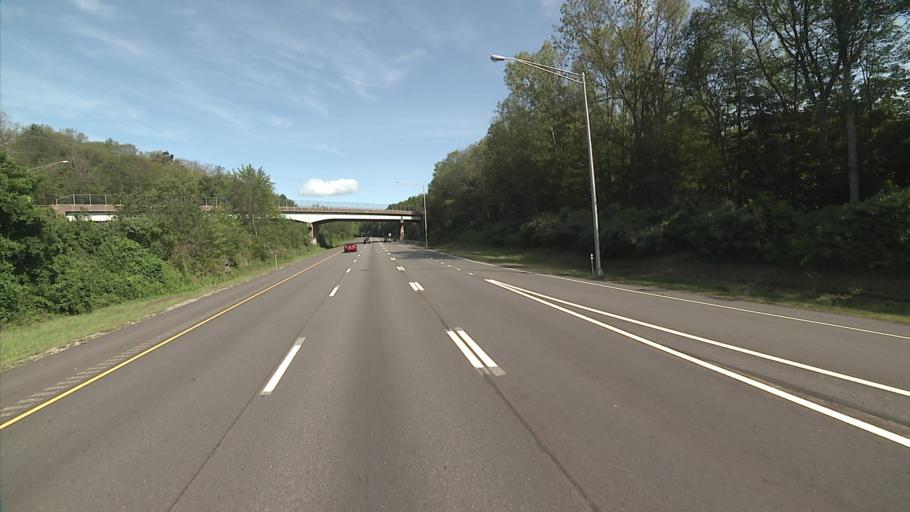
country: US
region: Connecticut
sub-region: Hartford County
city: Terramuggus
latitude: 41.6371
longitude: -72.4600
